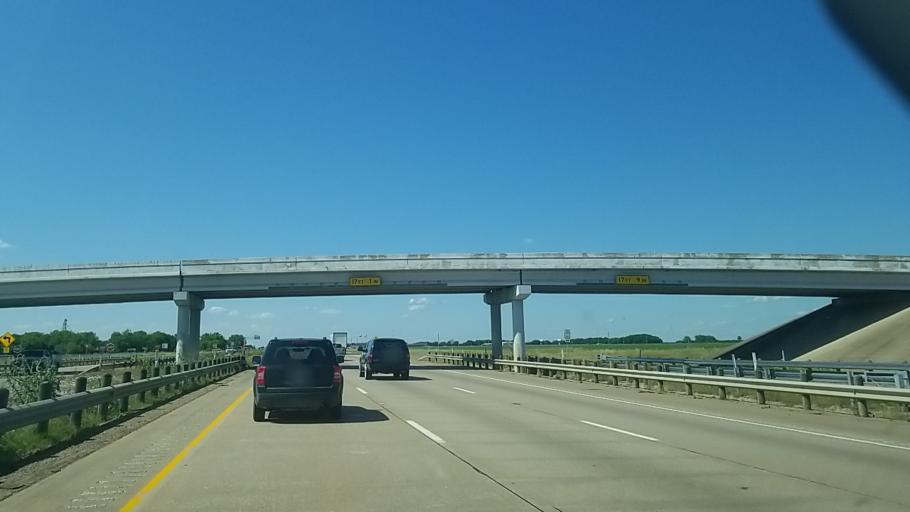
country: US
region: Texas
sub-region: Ellis County
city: Ferris
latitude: 32.4850
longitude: -96.6643
